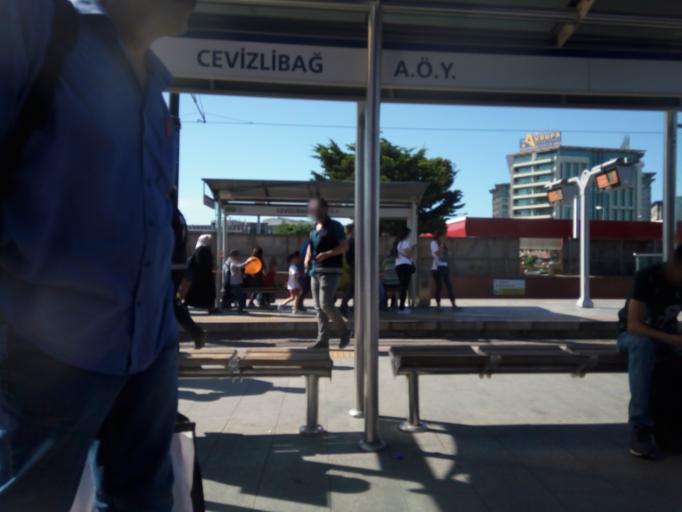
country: TR
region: Istanbul
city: Zeytinburnu
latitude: 41.0159
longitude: 28.9115
